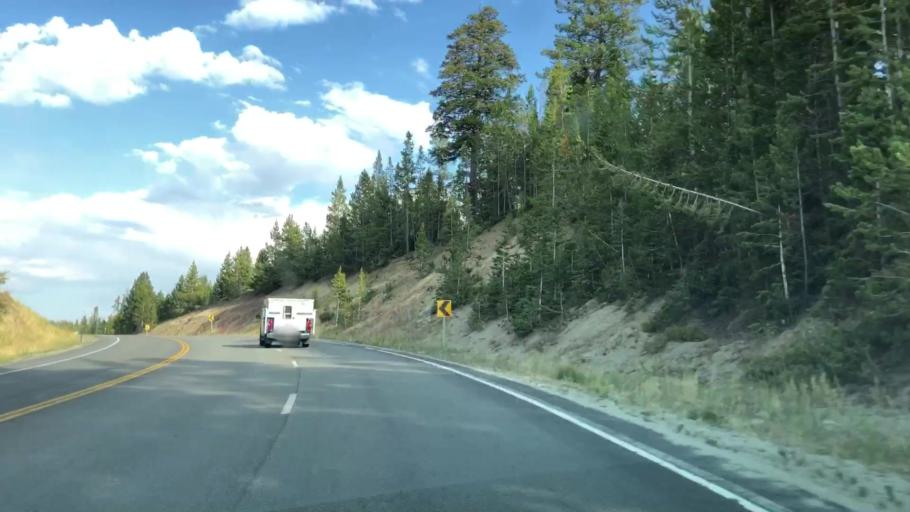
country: US
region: Wyoming
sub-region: Sublette County
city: Pinedale
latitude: 43.1323
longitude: -110.2038
